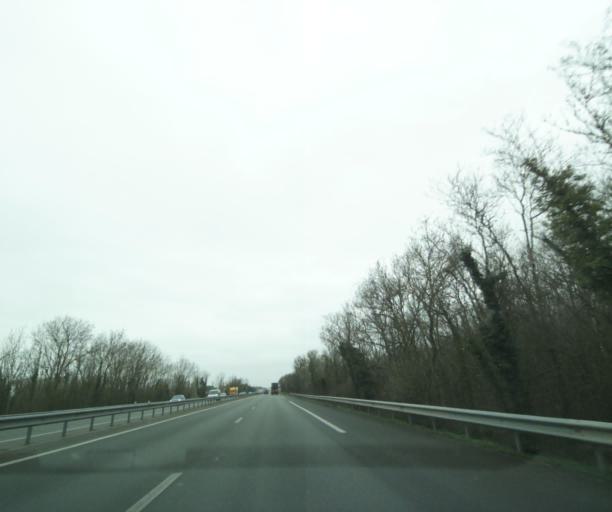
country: FR
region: Poitou-Charentes
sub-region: Departement de la Charente-Maritime
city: Angoulins
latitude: 46.0951
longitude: -1.0881
